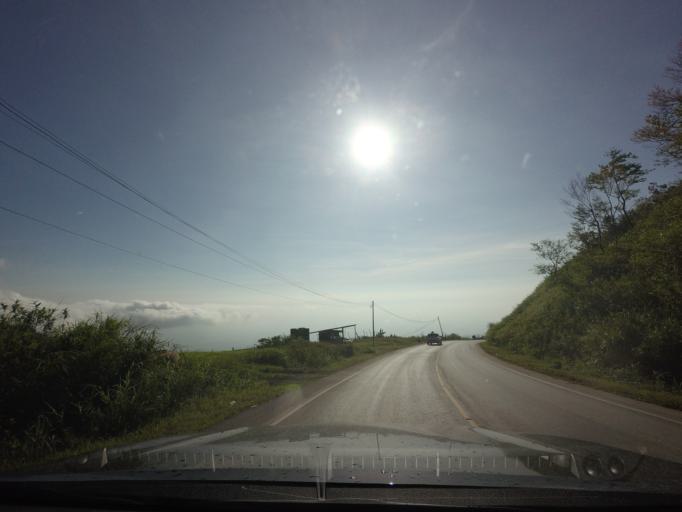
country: TH
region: Phetchabun
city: Lom Kao
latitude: 16.8848
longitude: 101.0989
